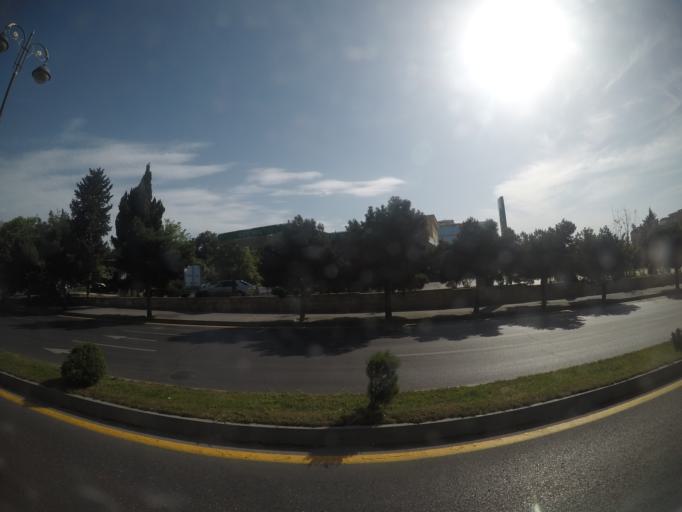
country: AZ
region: Baki
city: Badamdar
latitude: 40.3890
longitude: 49.8260
